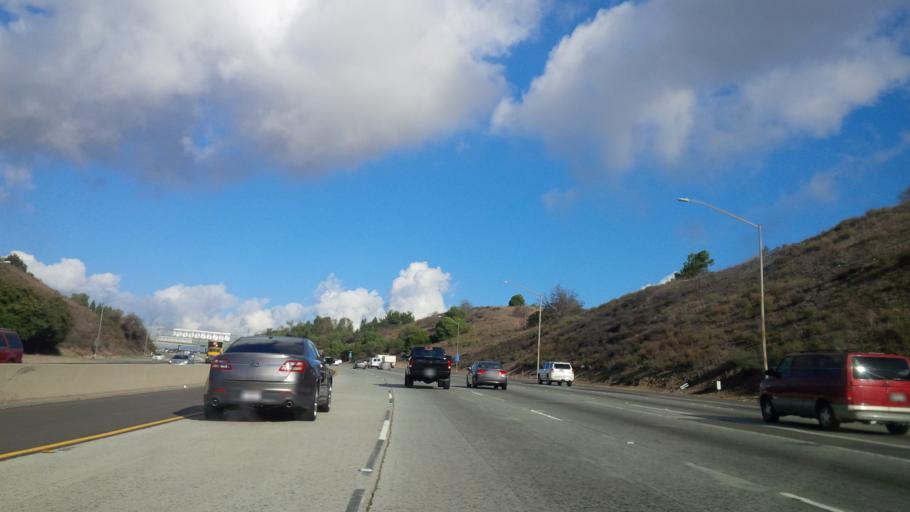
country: US
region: California
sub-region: Los Angeles County
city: San Dimas
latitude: 34.0718
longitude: -117.8086
